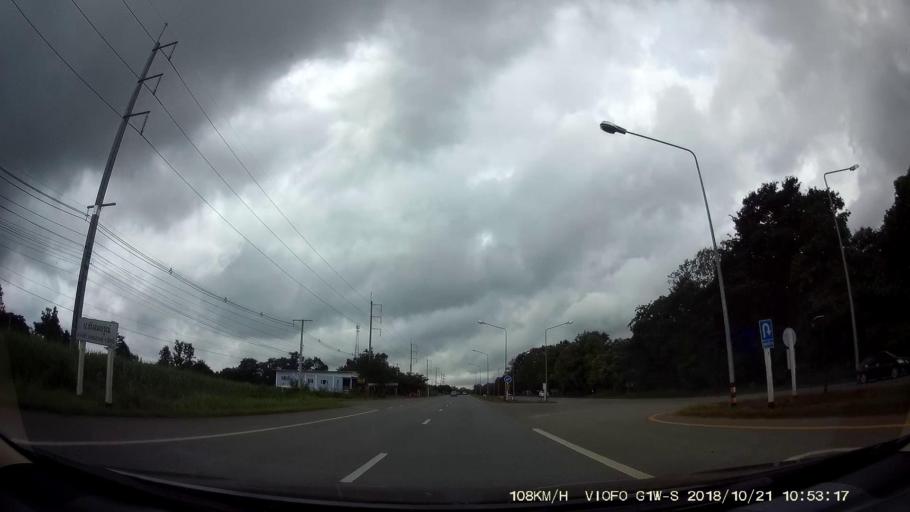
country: TH
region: Chaiyaphum
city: Khon Sawan
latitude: 15.9661
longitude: 102.1833
